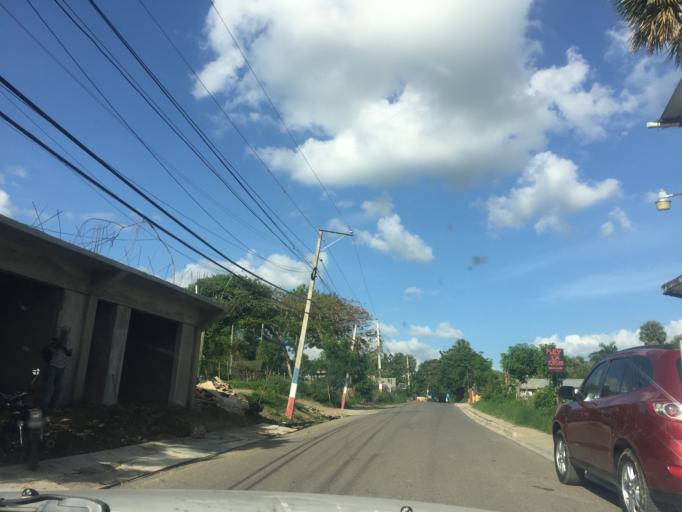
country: DO
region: Santiago
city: Tamboril
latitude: 19.4978
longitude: -70.6389
